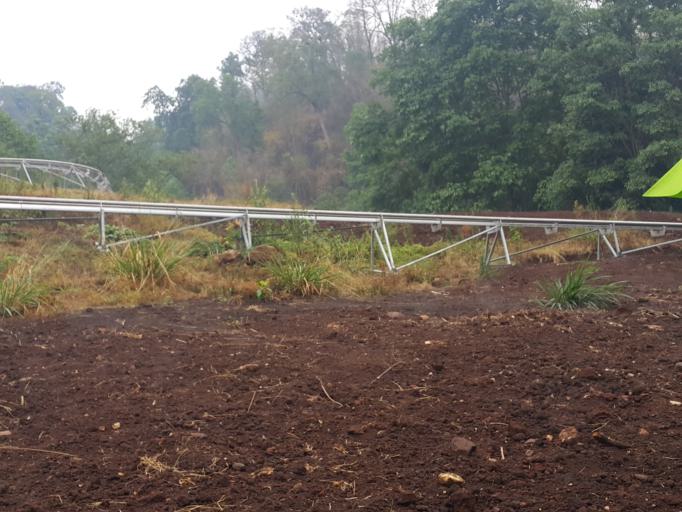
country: TH
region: Chiang Mai
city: Samoeng
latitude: 18.9148
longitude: 98.8211
